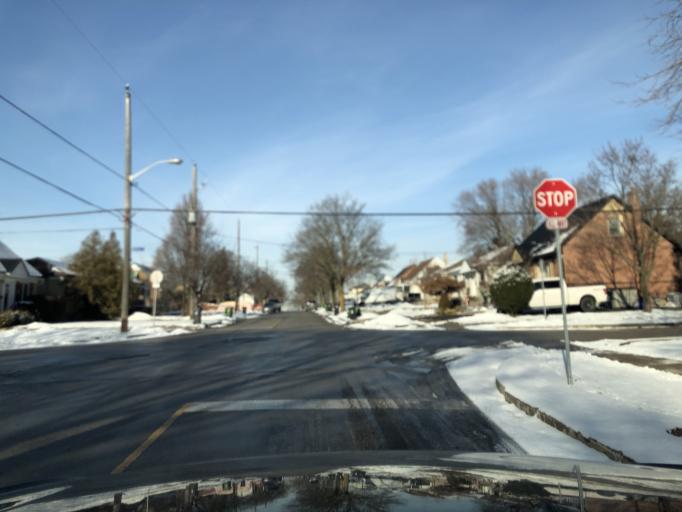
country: CA
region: Ontario
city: Etobicoke
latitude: 43.7095
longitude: -79.5163
